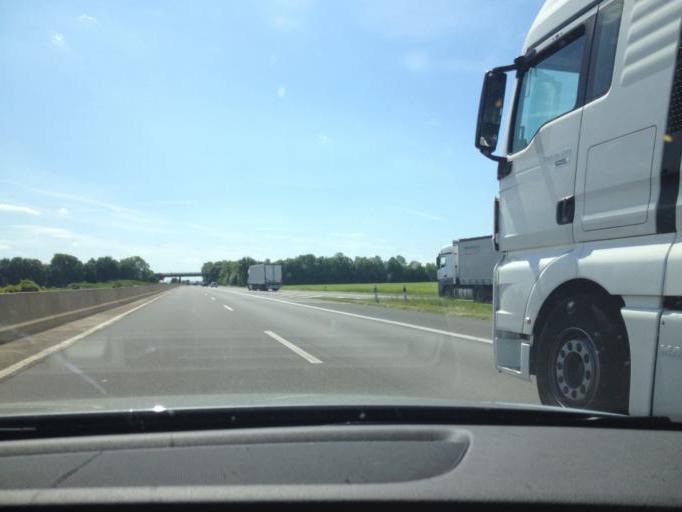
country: DE
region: North Rhine-Westphalia
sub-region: Regierungsbezirk Koln
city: Weilerswist
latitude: 50.7629
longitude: 6.8196
